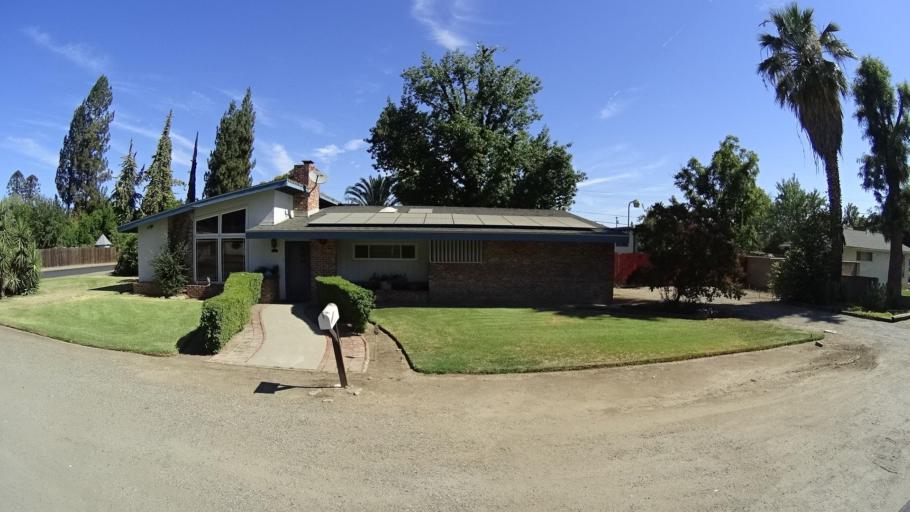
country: US
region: California
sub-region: Fresno County
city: Sunnyside
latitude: 36.7486
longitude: -119.7043
